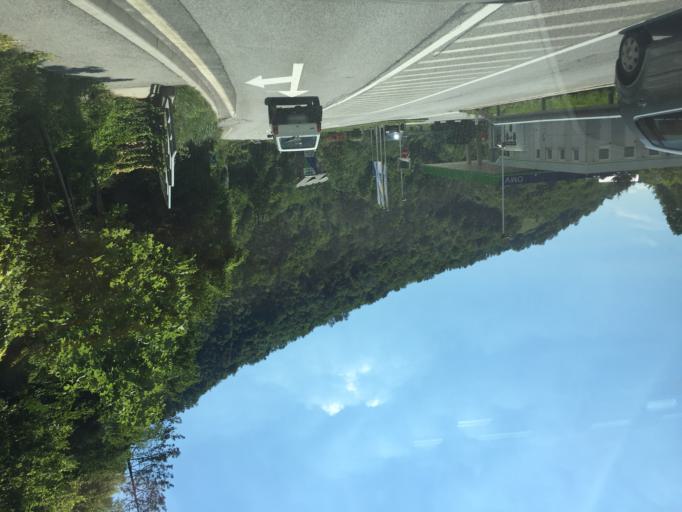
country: SI
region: Idrija
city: Spodnja Idrija
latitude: 46.0175
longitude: 14.0290
